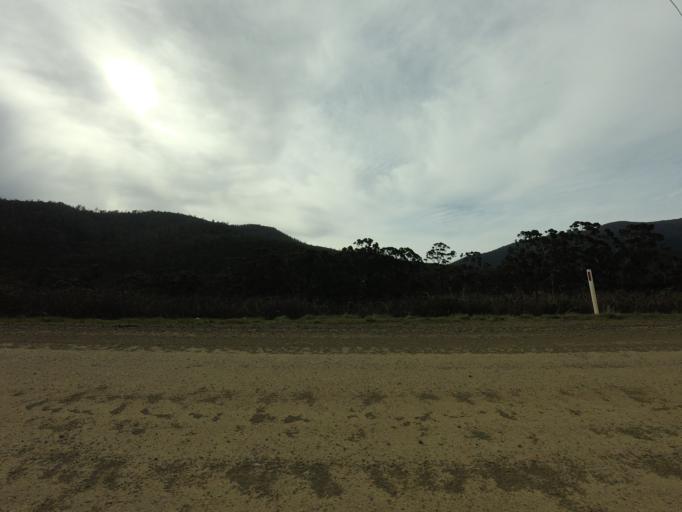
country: AU
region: Tasmania
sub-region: Huon Valley
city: Huonville
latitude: -43.0749
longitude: 147.0581
